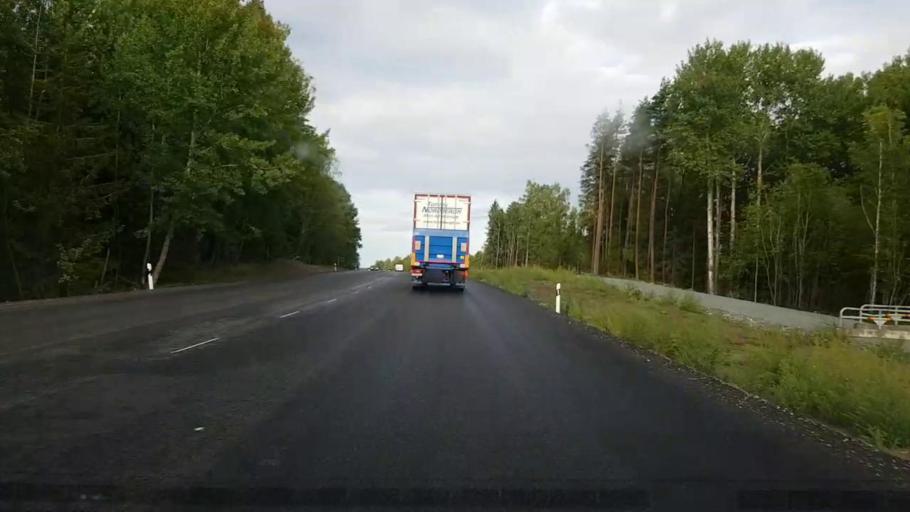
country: SE
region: Uppsala
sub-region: Enkopings Kommun
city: Irsta
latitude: 59.7015
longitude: 17.0115
